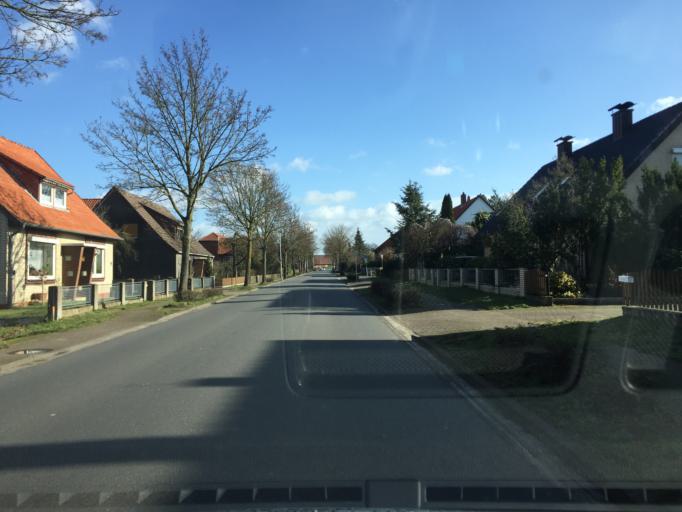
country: DE
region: Lower Saxony
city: Stolzenau
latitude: 52.5371
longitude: 9.0683
